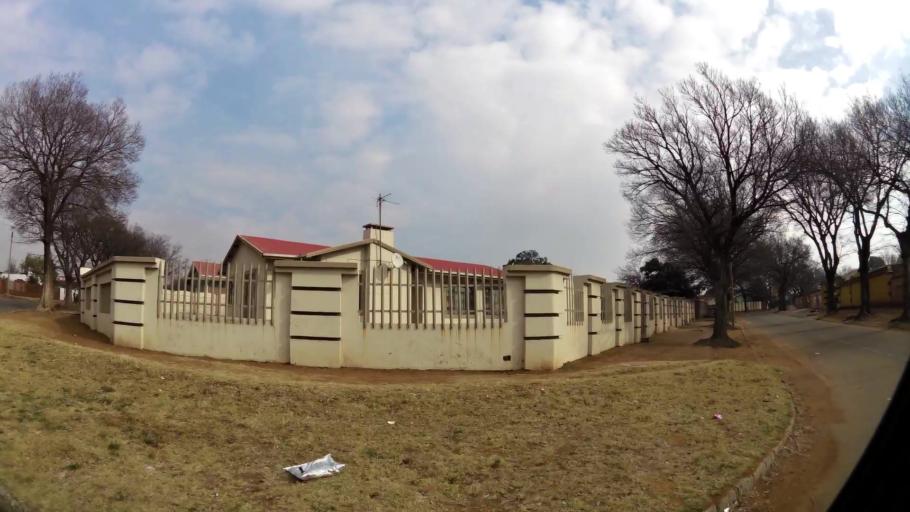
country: ZA
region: Gauteng
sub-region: Sedibeng District Municipality
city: Vanderbijlpark
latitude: -26.6792
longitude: 27.8348
